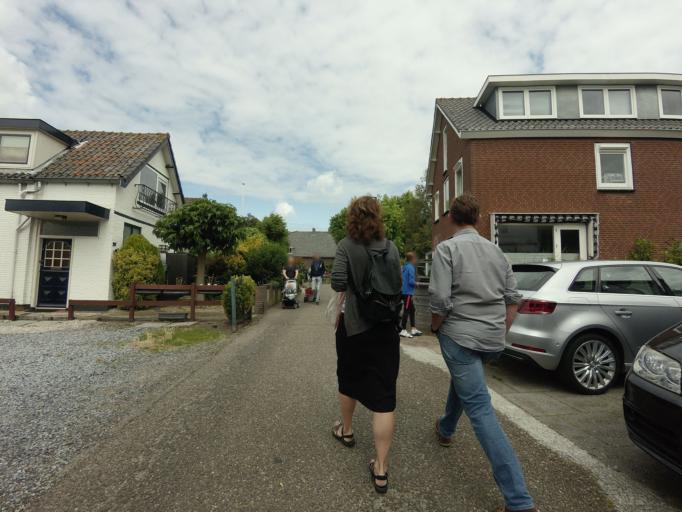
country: NL
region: South Holland
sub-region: Gemeente Teylingen
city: Sassenheim
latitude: 52.2155
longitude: 4.5585
